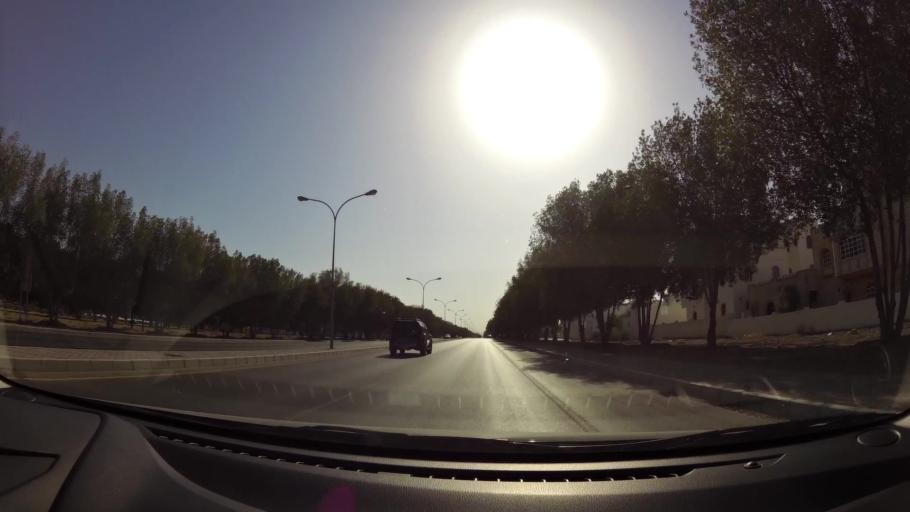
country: OM
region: Muhafazat Masqat
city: As Sib al Jadidah
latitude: 23.6151
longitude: 58.2119
